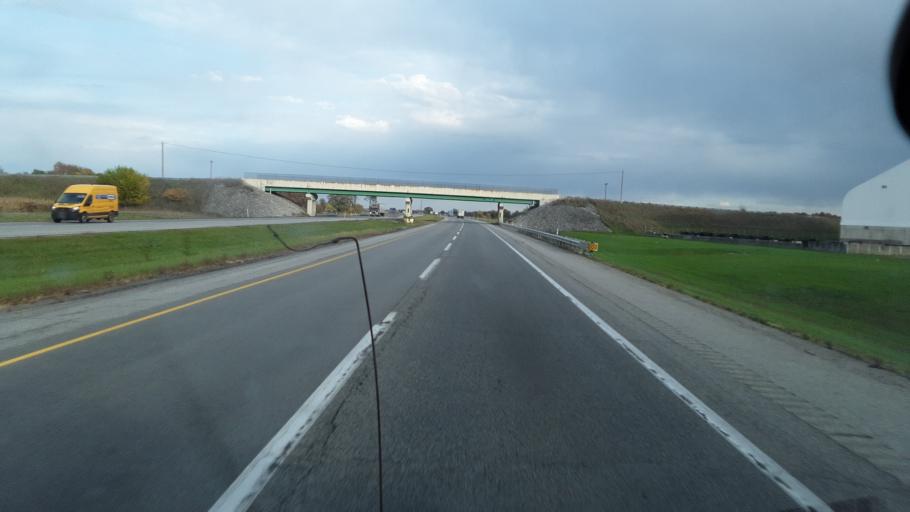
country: US
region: Michigan
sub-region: Saint Joseph County
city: White Pigeon
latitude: 41.7464
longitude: -85.5454
